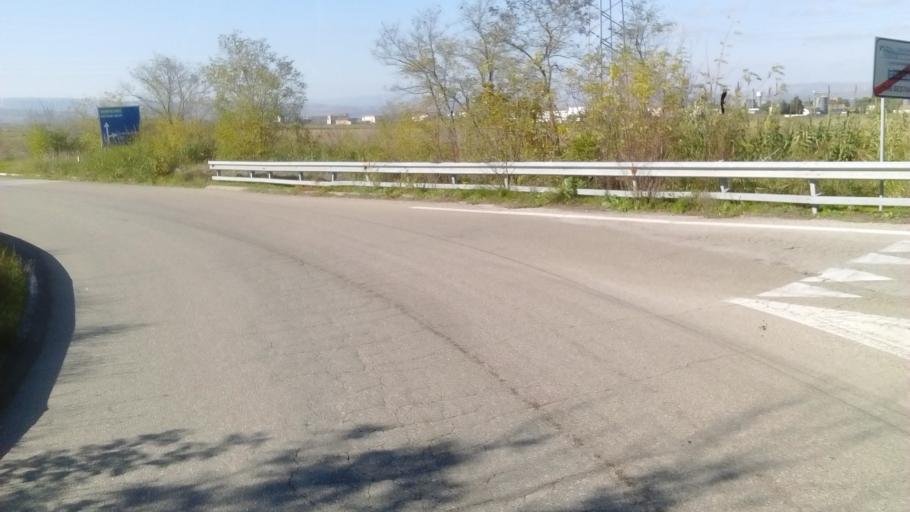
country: IT
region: Basilicate
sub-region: Provincia di Potenza
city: Melfi
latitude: 41.0662
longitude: 15.6841
